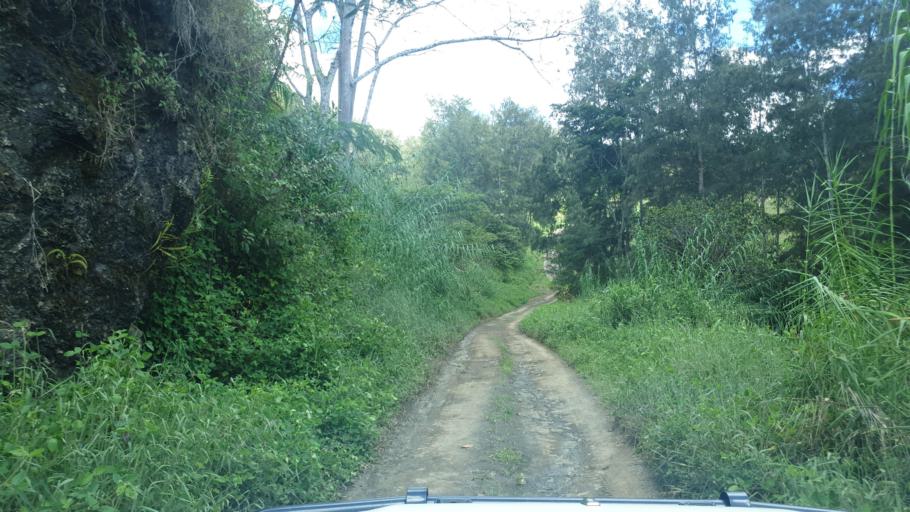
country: PG
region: Chimbu
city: Kundiawa
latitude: -6.2578
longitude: 145.1379
